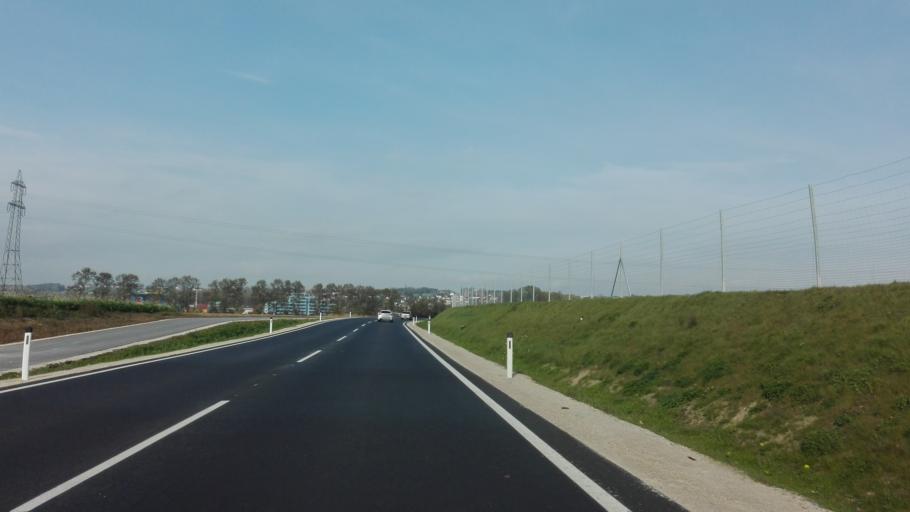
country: AT
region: Lower Austria
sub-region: Politischer Bezirk Amstetten
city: Ennsdorf
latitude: 48.2270
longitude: 14.5137
